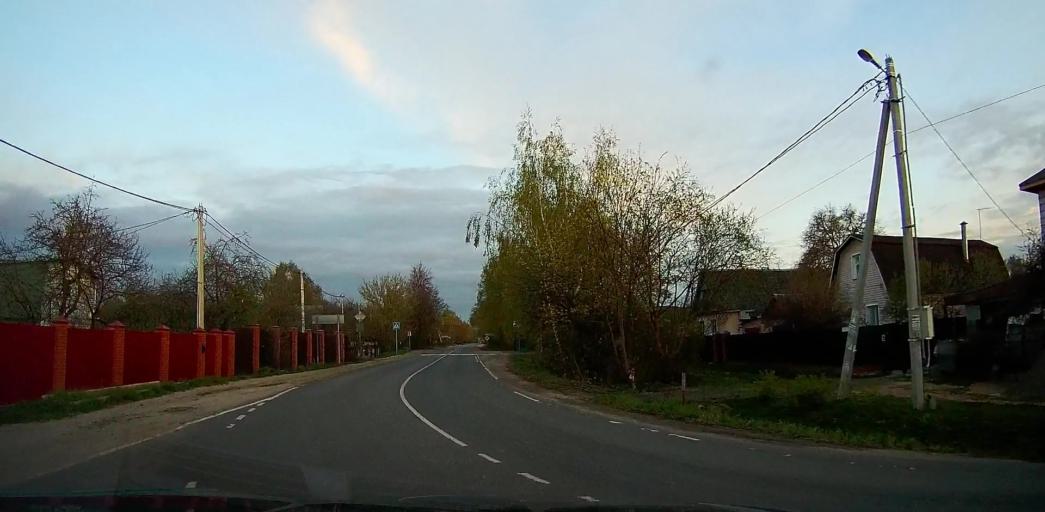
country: RU
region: Moskovskaya
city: Peski
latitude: 55.2078
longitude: 38.7392
